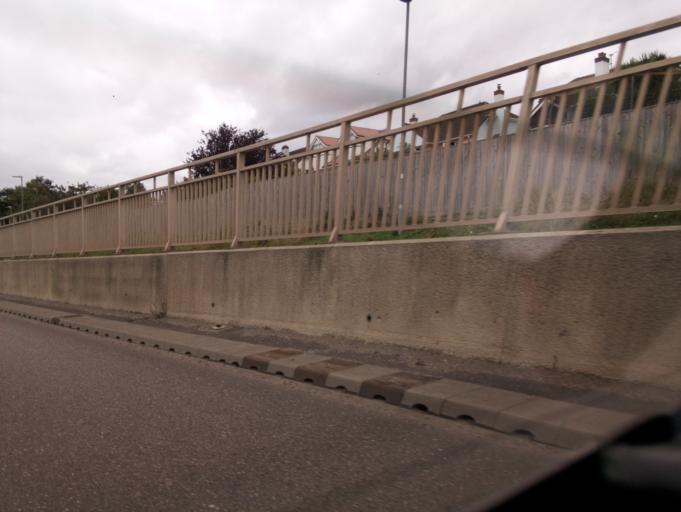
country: GB
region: England
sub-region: Devon
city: Kingskerswell
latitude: 50.5190
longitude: -3.5909
